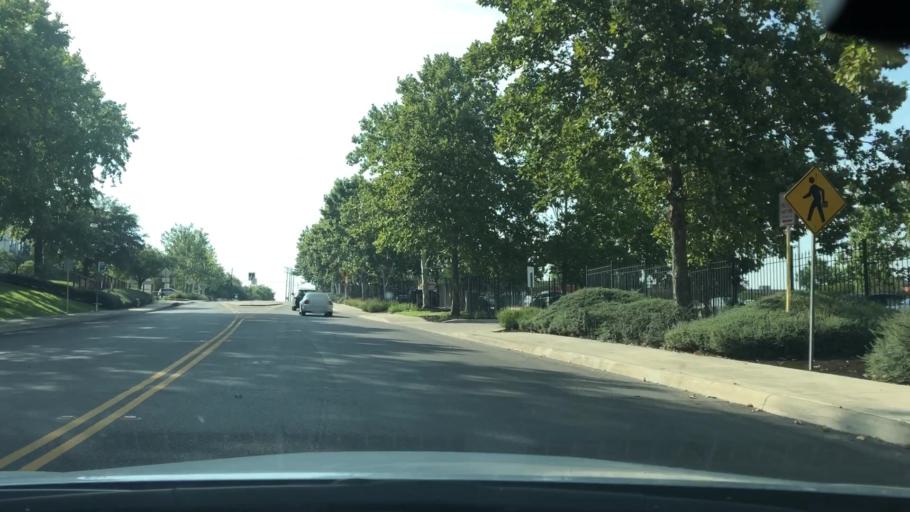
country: US
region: Texas
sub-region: Bexar County
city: Hollywood Park
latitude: 29.5532
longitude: -98.4643
